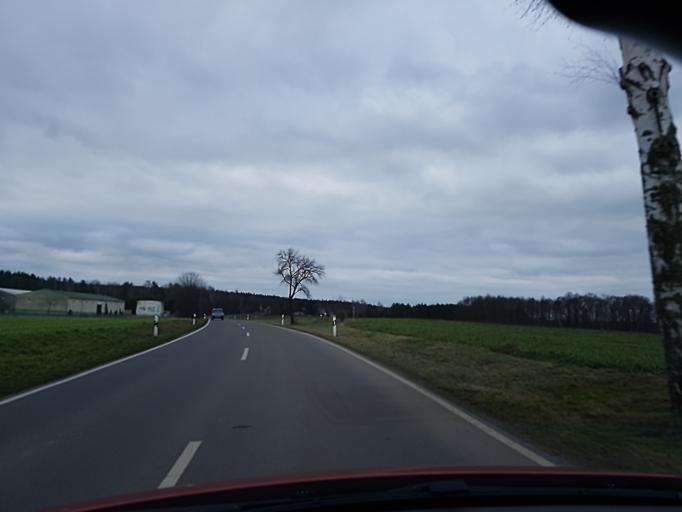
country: DE
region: Brandenburg
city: Bad Liebenwerda
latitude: 51.5569
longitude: 13.4184
